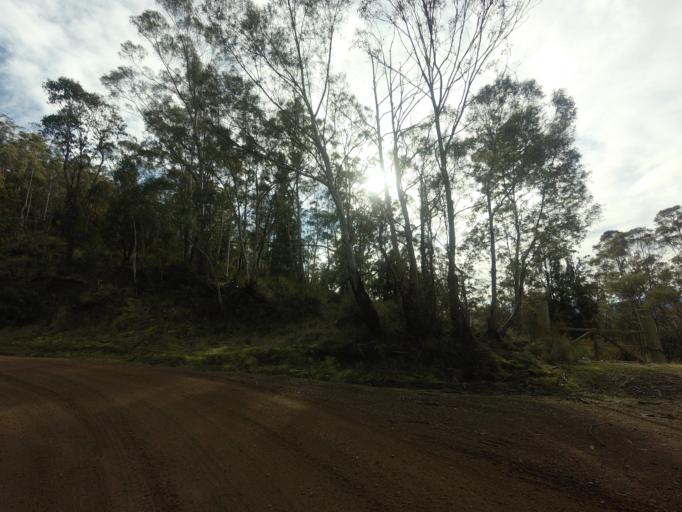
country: AU
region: Tasmania
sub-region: Derwent Valley
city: New Norfolk
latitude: -42.7882
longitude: 146.9426
